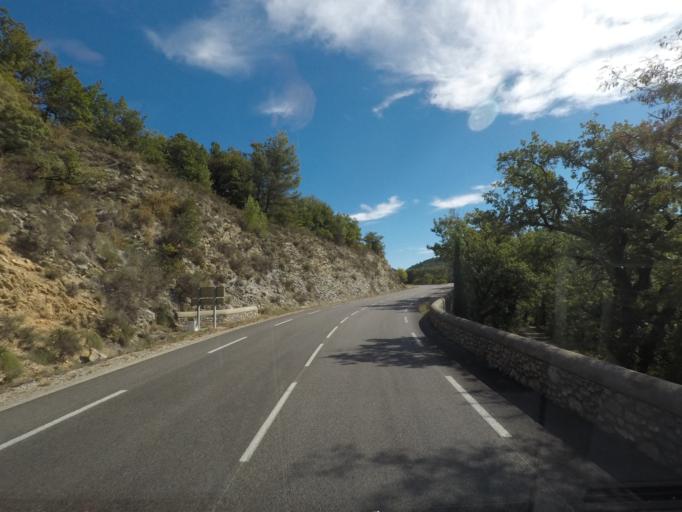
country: FR
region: Rhone-Alpes
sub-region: Departement de la Drome
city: Nyons
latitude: 44.3901
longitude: 5.2223
